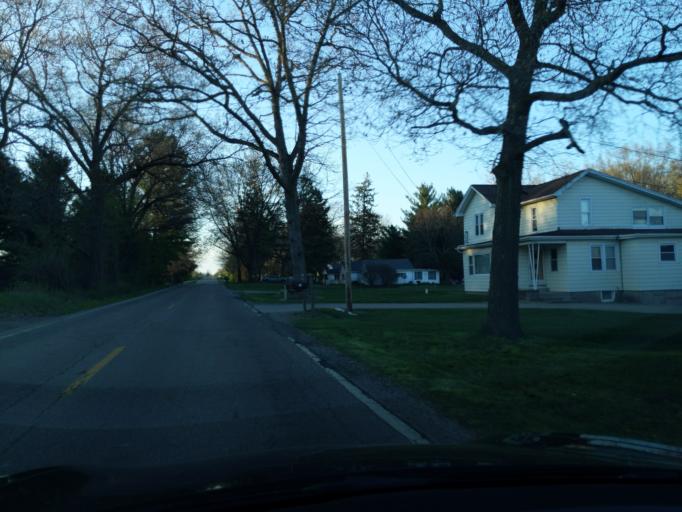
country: US
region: Michigan
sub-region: Jackson County
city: Jackson
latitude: 42.2658
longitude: -84.4832
